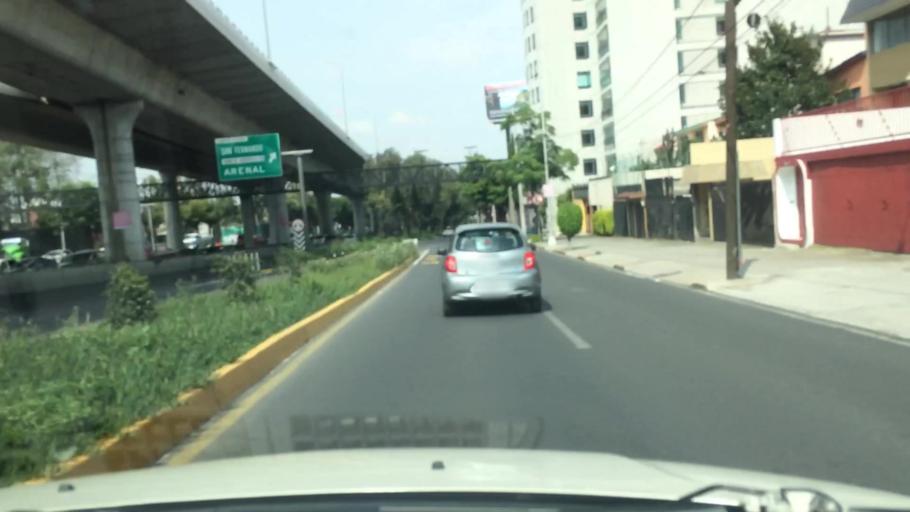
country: MX
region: Mexico City
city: Tlalpan
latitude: 19.2797
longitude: -99.1636
